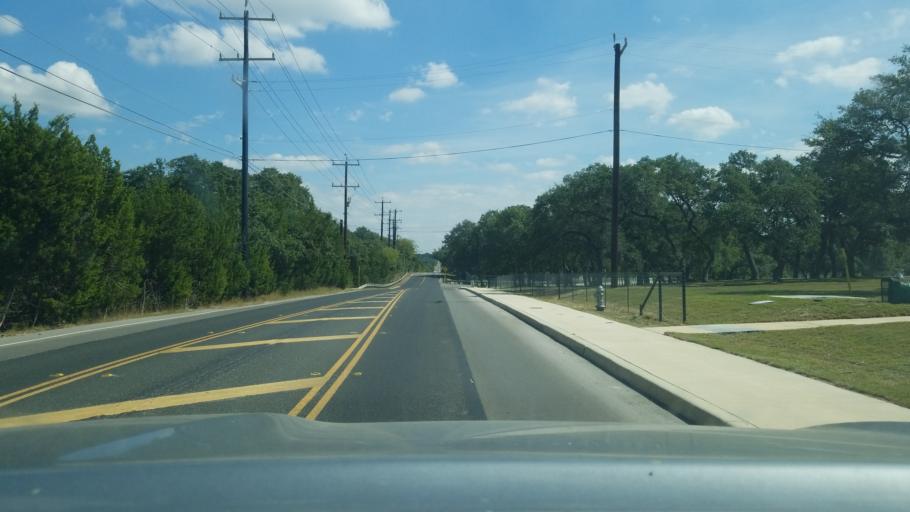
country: US
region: Texas
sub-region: Bexar County
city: Fair Oaks Ranch
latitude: 29.7311
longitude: -98.6580
